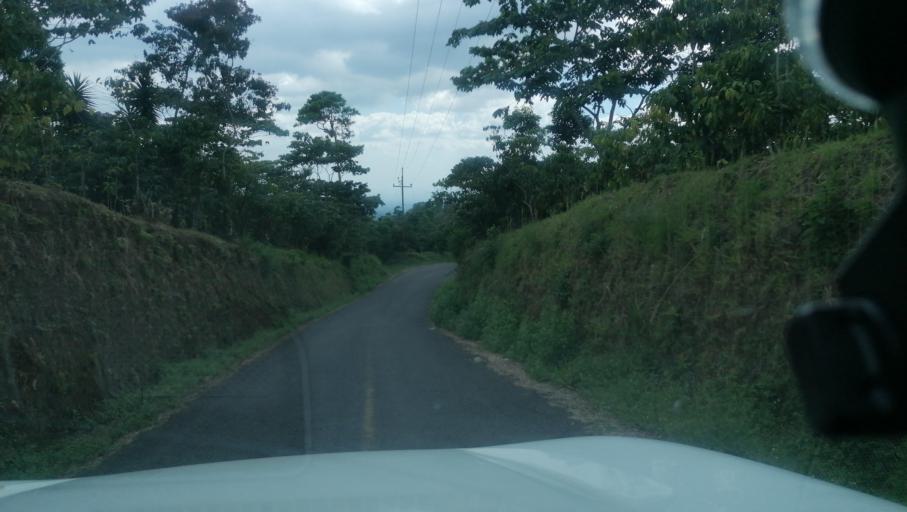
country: MX
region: Chiapas
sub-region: Cacahoatan
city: Benito Juarez
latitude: 15.0624
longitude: -92.1503
